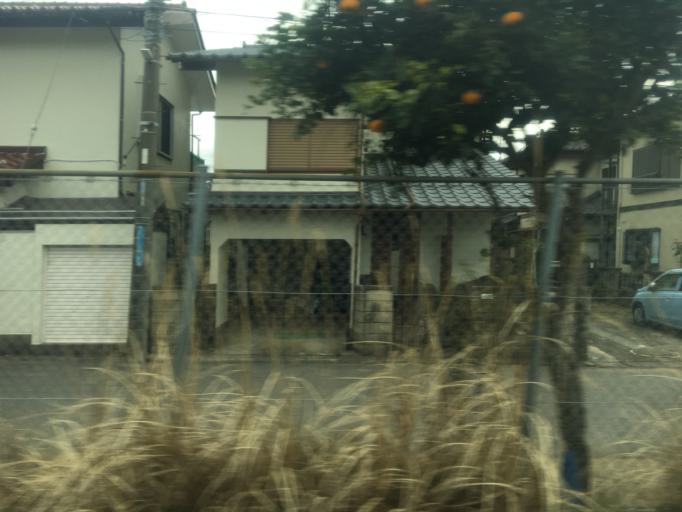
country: JP
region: Chiba
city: Abiko
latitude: 35.8686
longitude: 140.0442
